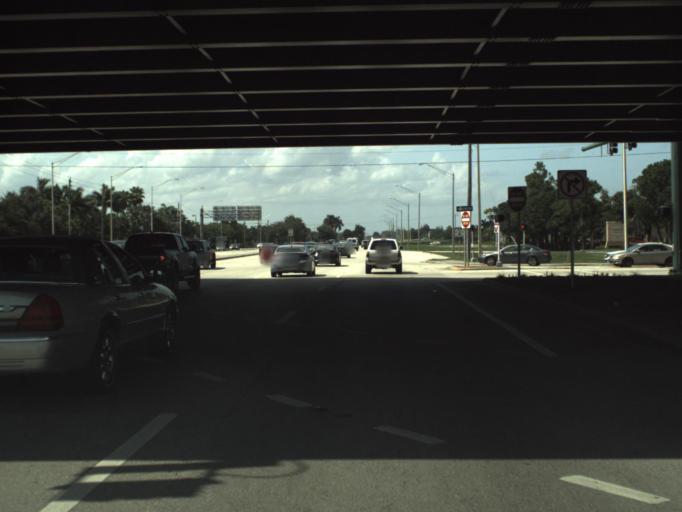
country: US
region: Florida
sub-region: Palm Beach County
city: Royal Palm Beach
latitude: 26.6804
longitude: -80.2022
